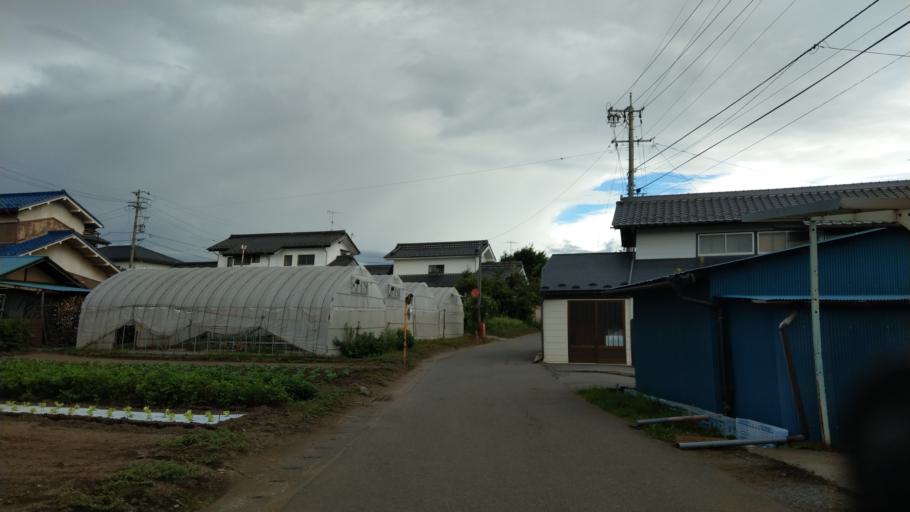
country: JP
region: Nagano
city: Komoro
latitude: 36.3032
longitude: 138.4700
